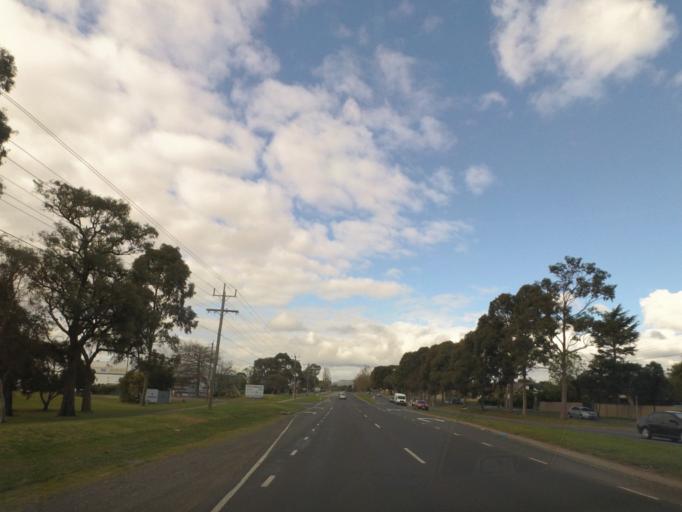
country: AU
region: Victoria
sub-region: Maroondah
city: Heathmont
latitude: -37.8444
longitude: 145.2436
